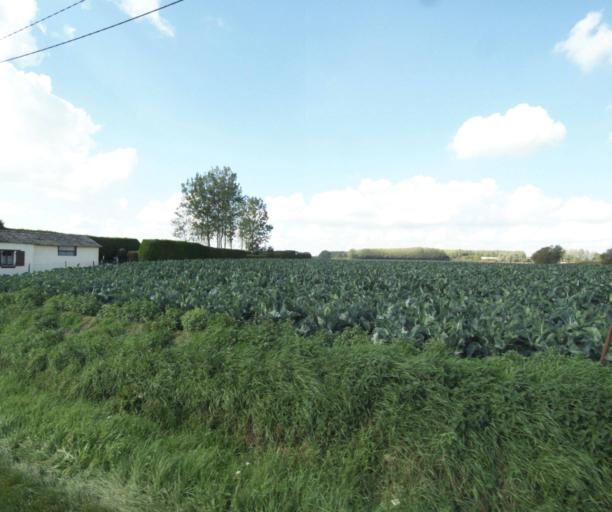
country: FR
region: Nord-Pas-de-Calais
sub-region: Departement du Nord
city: Illies
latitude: 50.5775
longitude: 2.8210
